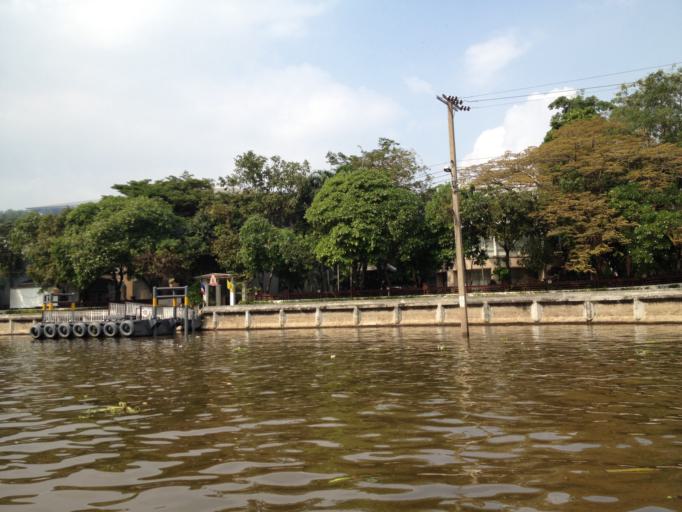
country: TH
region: Nonthaburi
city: Bang Kruai
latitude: 13.7930
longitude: 100.4686
